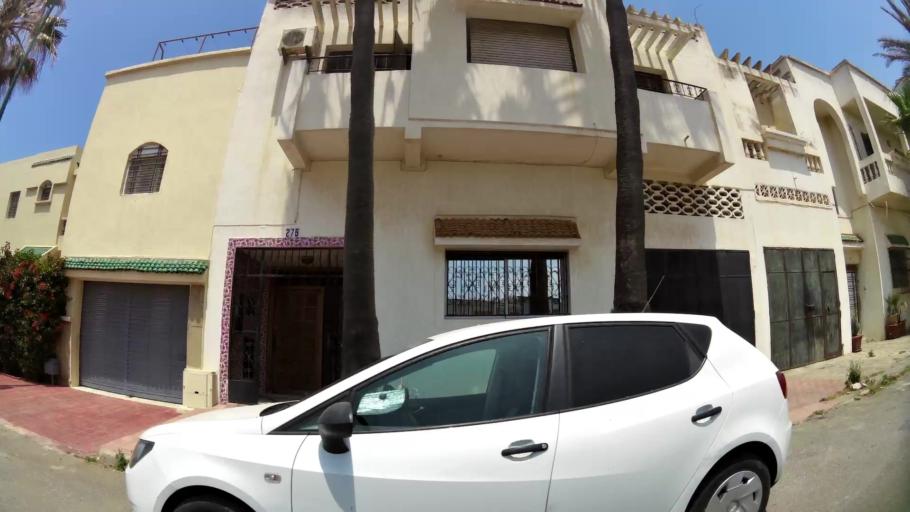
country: MA
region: Rabat-Sale-Zemmour-Zaer
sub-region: Skhirate-Temara
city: Temara
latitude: 33.9774
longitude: -6.8965
